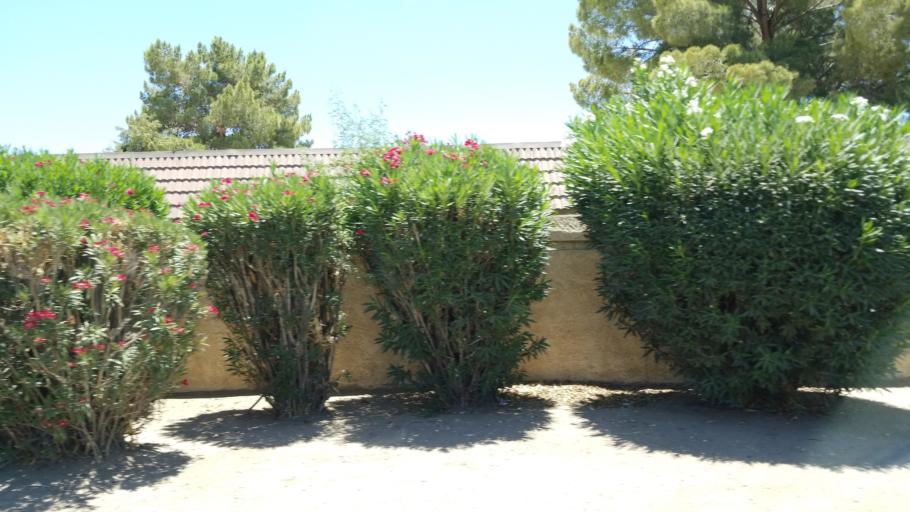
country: US
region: Arizona
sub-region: Maricopa County
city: Tolleson
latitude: 33.5087
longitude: -112.2525
